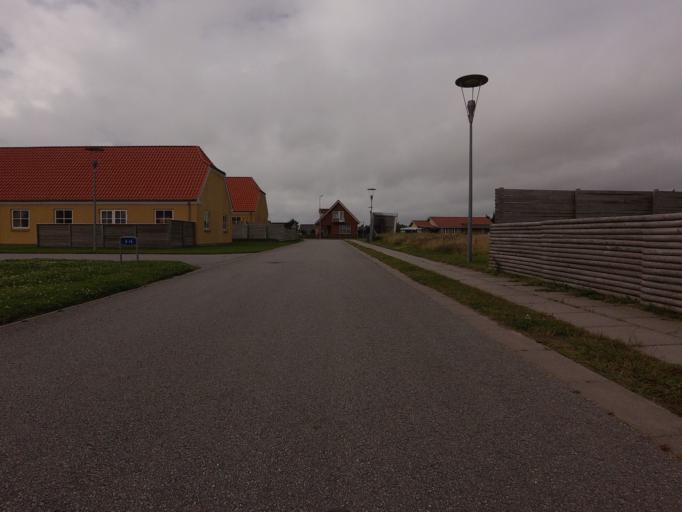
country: DK
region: North Denmark
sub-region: Jammerbugt Kommune
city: Pandrup
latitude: 57.3730
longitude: 9.7229
